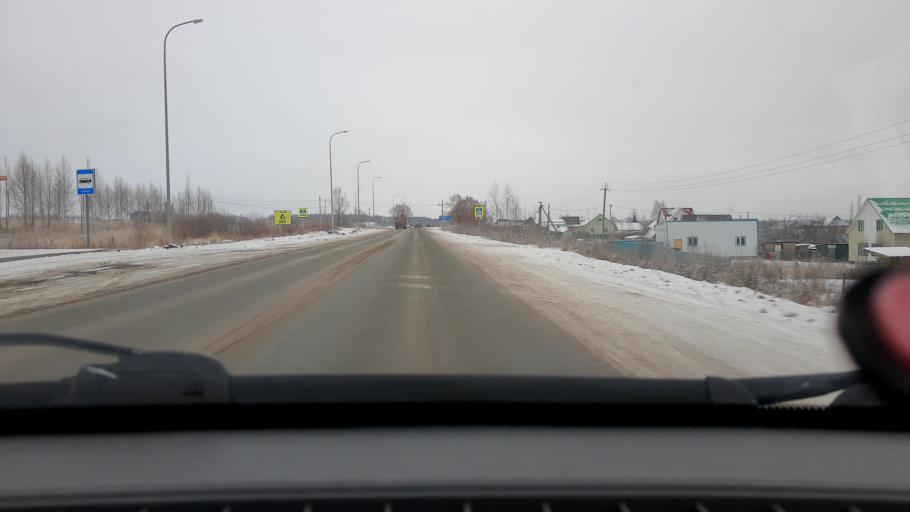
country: RU
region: Bashkortostan
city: Iglino
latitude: 54.8433
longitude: 56.4009
